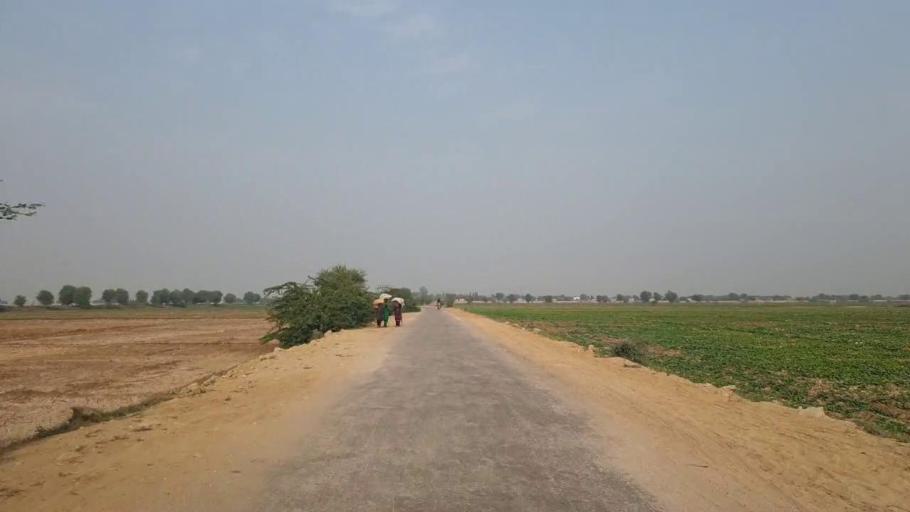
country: PK
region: Sindh
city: Sann
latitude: 26.0632
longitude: 68.1096
